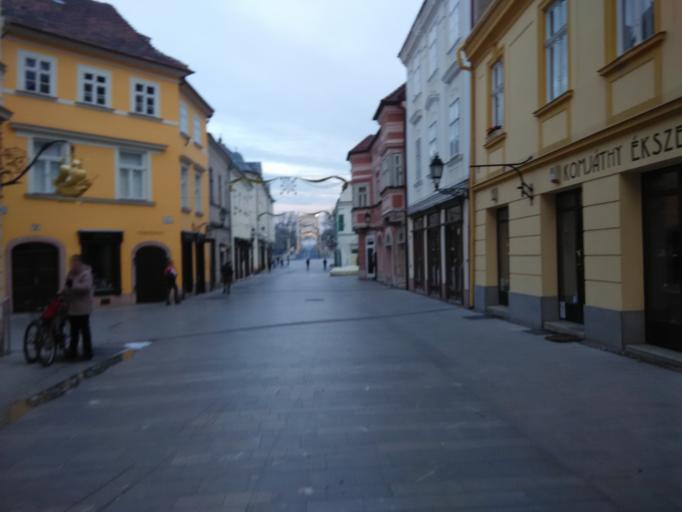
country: HU
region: Gyor-Moson-Sopron
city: Gyor
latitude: 47.6887
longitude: 17.6335
